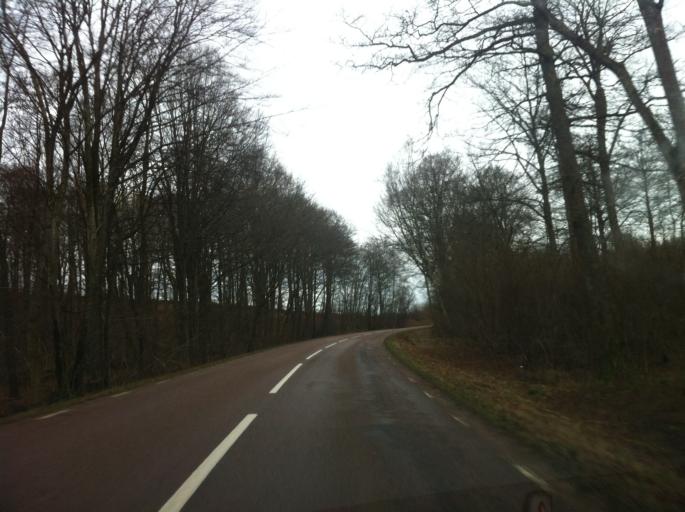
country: SE
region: Skane
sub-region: Svalovs Kommun
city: Kagerod
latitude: 56.0347
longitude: 13.0994
